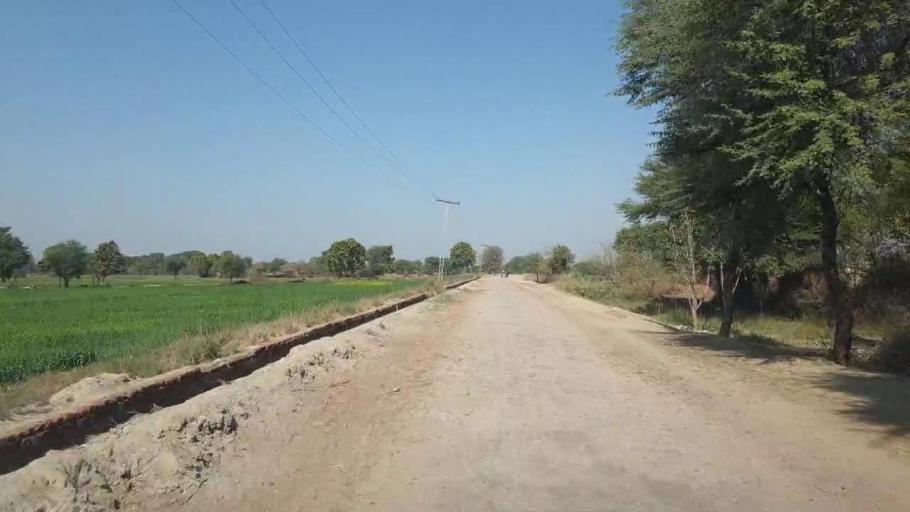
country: PK
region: Sindh
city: Chambar
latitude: 25.2955
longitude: 68.6918
